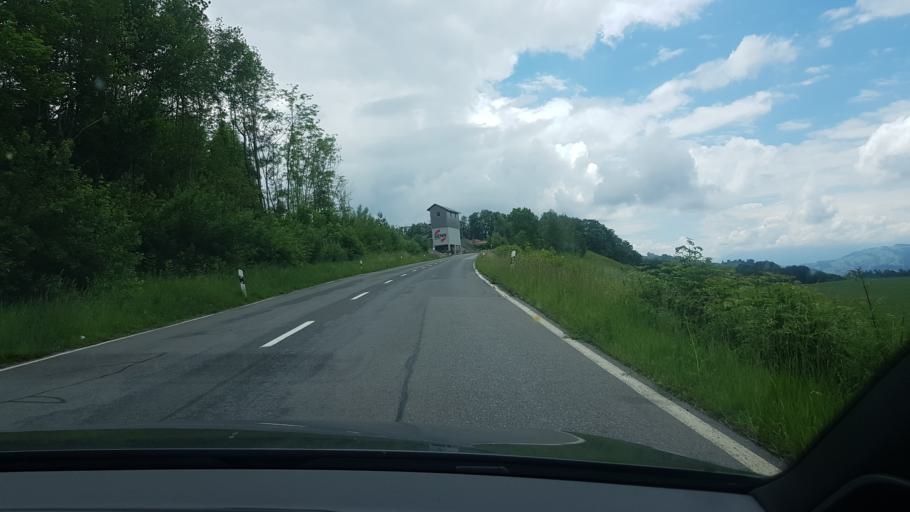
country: CH
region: Zug
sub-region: Zug
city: Menzingen
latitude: 47.1925
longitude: 8.5709
